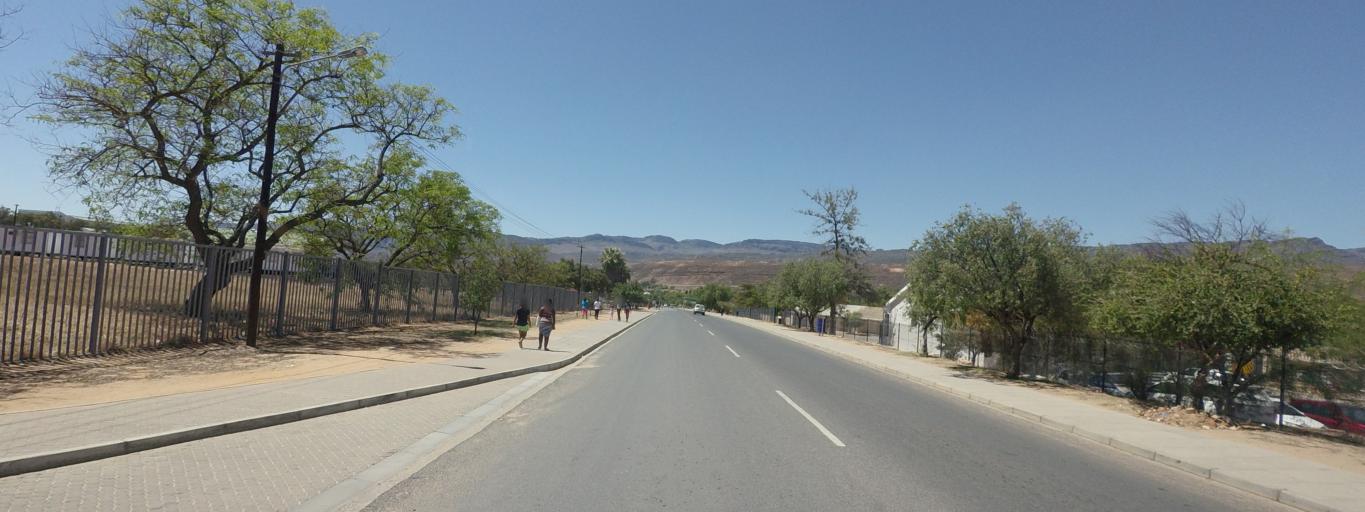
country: ZA
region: Western Cape
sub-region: West Coast District Municipality
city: Clanwilliam
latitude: -32.1851
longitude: 18.8915
